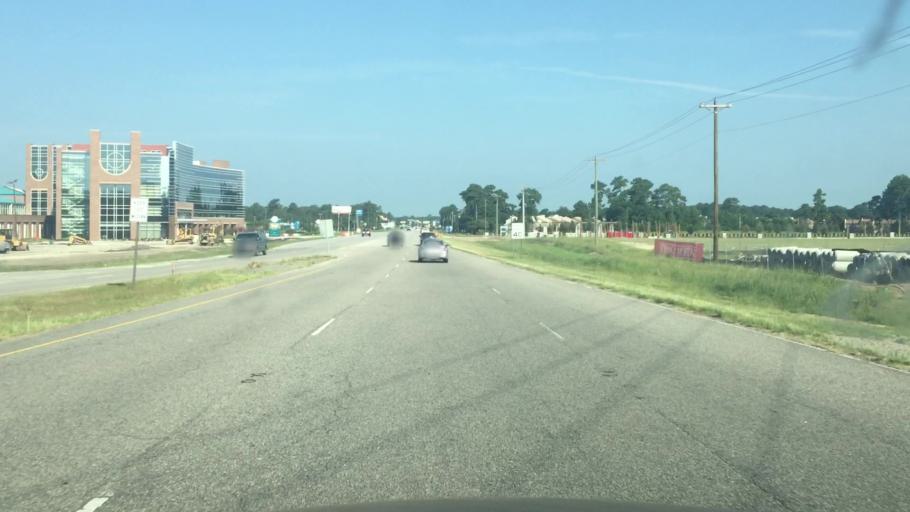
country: US
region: South Carolina
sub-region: Horry County
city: Little River
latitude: 33.8655
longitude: -78.6606
